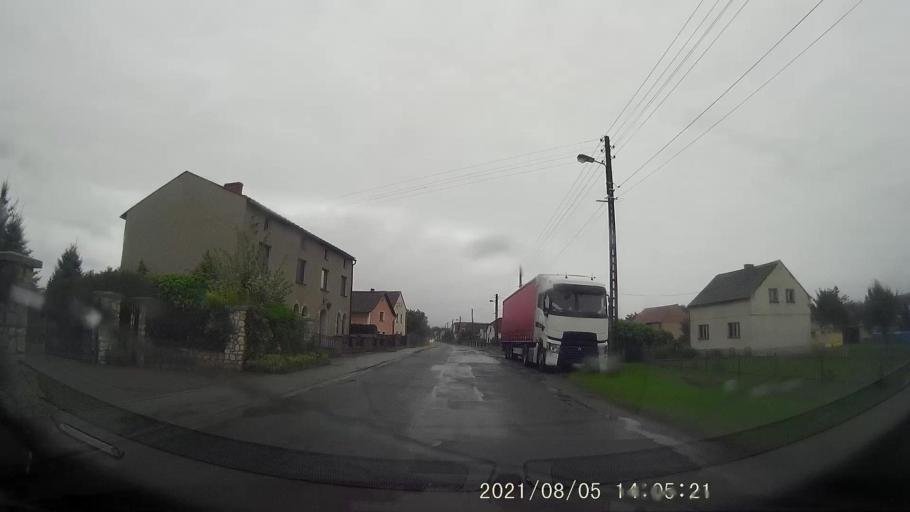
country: PL
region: Opole Voivodeship
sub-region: Powiat krapkowicki
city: Strzeleczki
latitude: 50.4643
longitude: 17.8541
